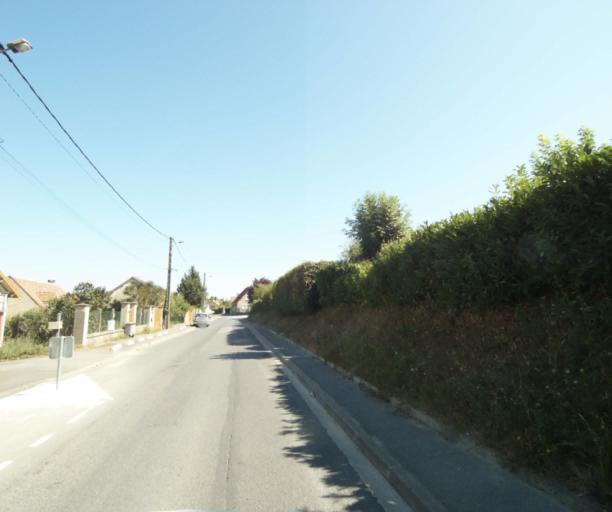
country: FR
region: Ile-de-France
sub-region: Departement de l'Essonne
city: Itteville
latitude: 48.5206
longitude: 2.3490
